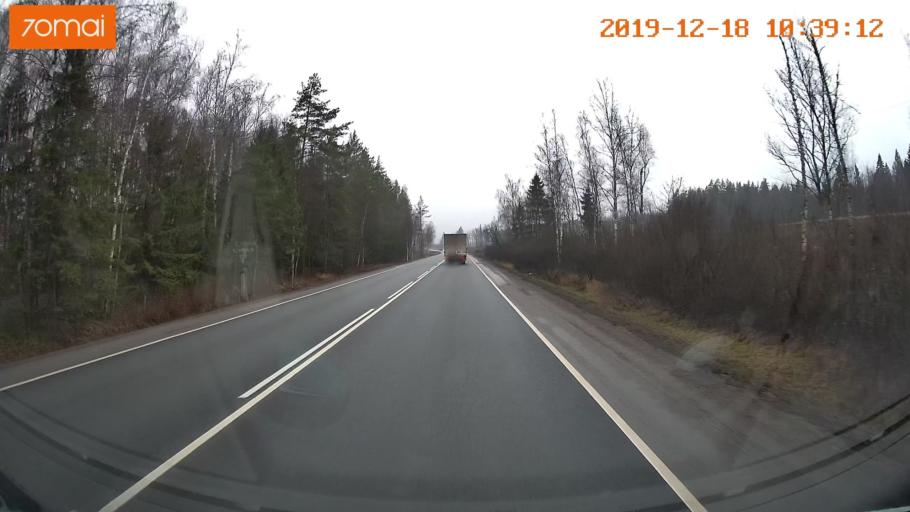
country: RU
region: Moskovskaya
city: Aprelevka
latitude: 55.4415
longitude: 37.1446
